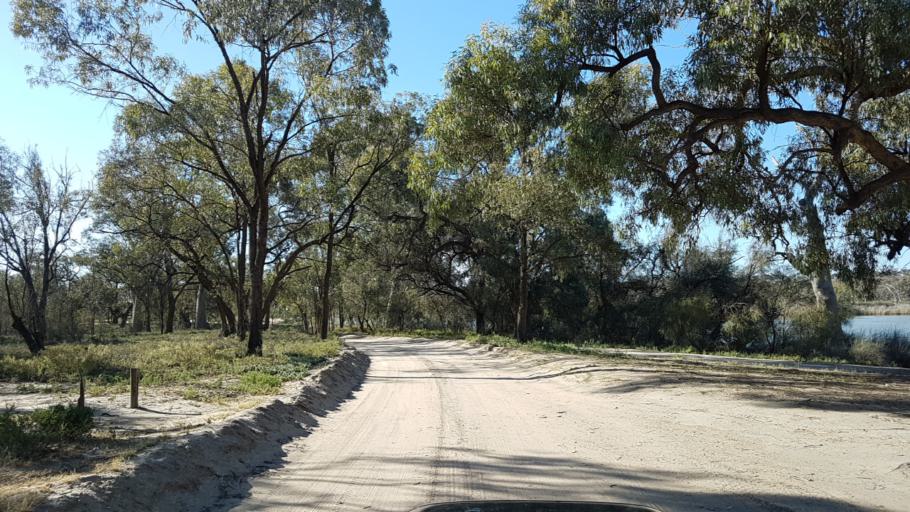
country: AU
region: South Australia
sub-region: Loxton Waikerie
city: Waikerie
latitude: -34.1617
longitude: 140.0321
